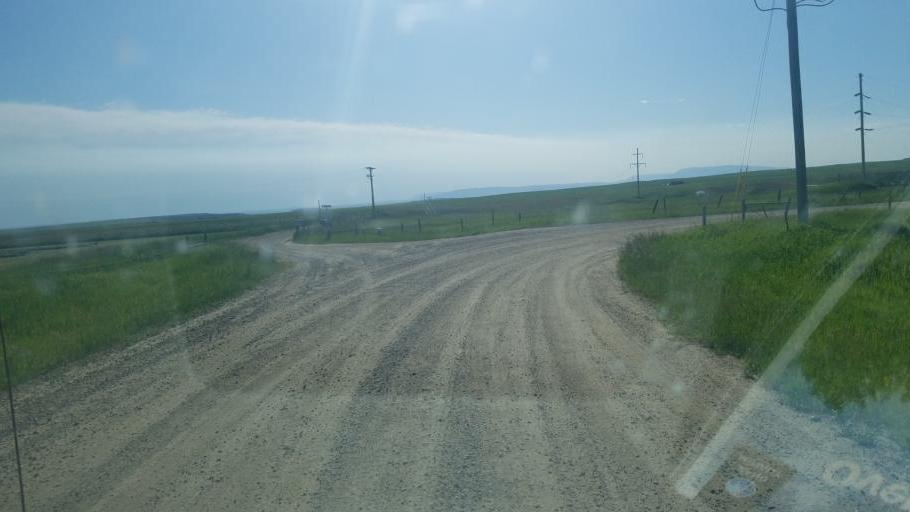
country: US
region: Montana
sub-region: Carbon County
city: Red Lodge
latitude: 45.3490
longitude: -109.1563
